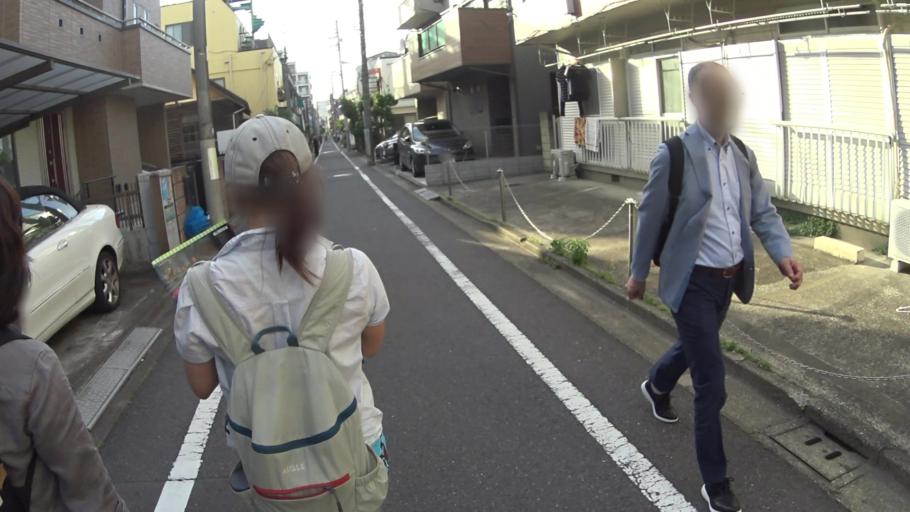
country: JP
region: Tokyo
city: Tokyo
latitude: 35.7313
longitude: 139.6810
